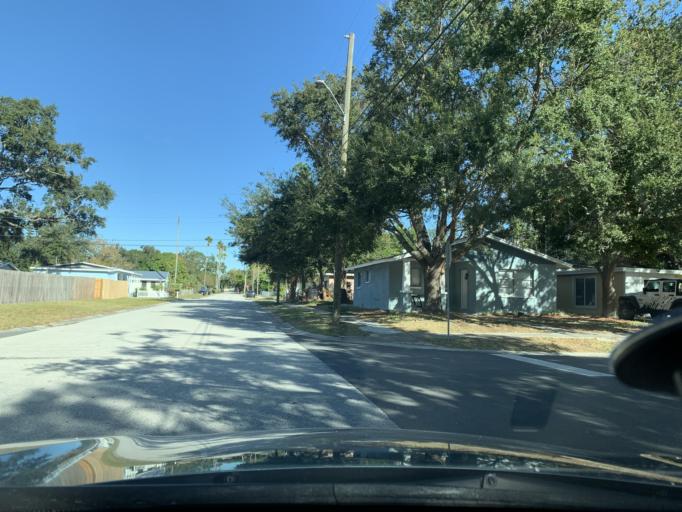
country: US
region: Florida
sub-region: Pinellas County
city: Gulfport
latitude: 27.7562
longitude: -82.7018
